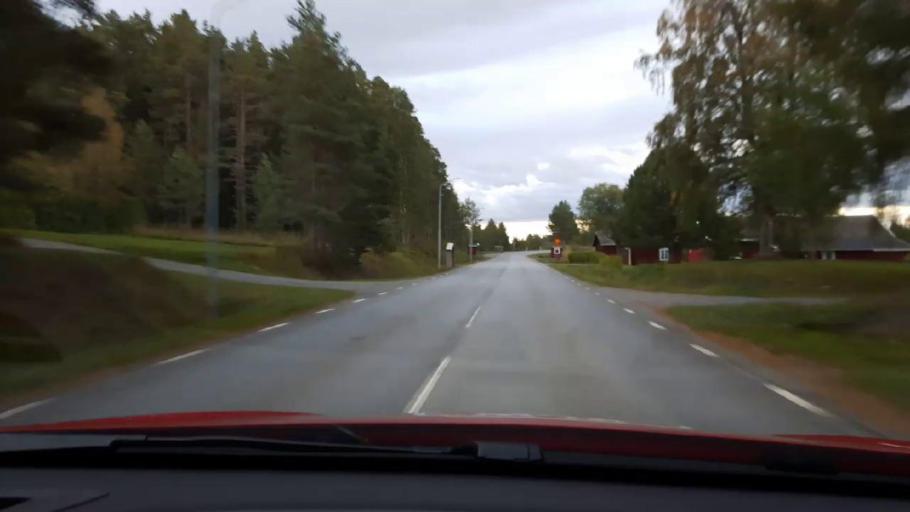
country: SE
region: Jaemtland
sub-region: Bergs Kommun
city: Hoverberg
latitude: 62.9777
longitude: 14.4825
